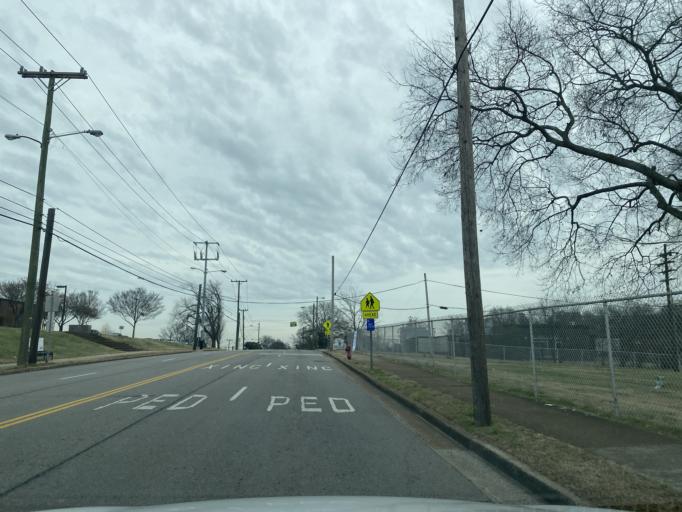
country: US
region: Tennessee
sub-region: Davidson County
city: Nashville
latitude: 36.1419
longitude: -86.7841
